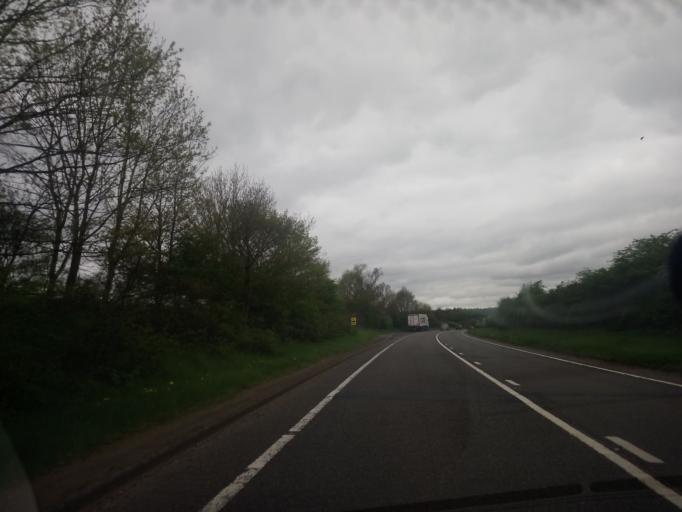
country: GB
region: England
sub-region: Telford and Wrekin
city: Chetwynd
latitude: 52.7935
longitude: -2.4092
